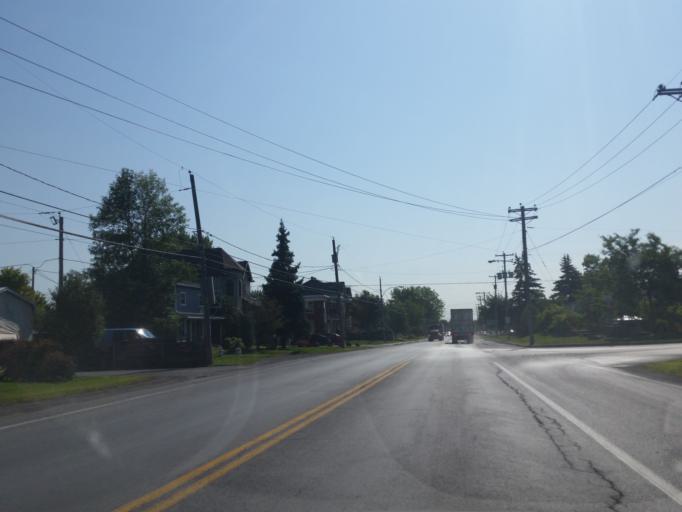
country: CA
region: Quebec
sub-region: Monteregie
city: Saint-Jean-sur-Richelieu
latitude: 45.3036
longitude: -73.2963
